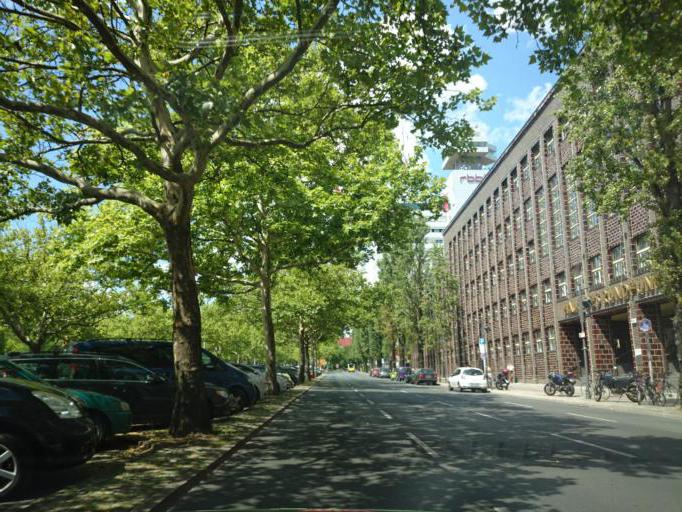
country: DE
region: Berlin
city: Westend
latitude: 52.5076
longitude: 13.2765
